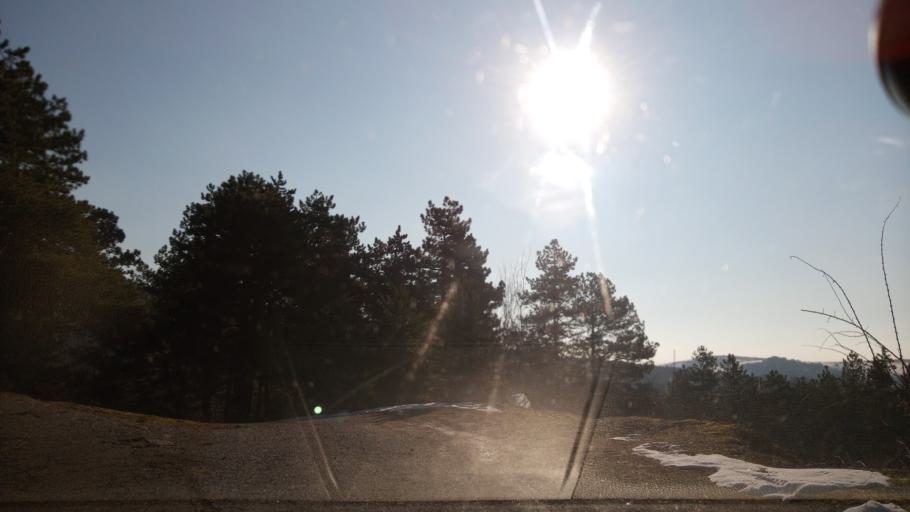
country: BG
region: Sofia-Capital
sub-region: Stolichna Obshtina
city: Bukhovo
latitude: 42.7947
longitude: 23.5318
